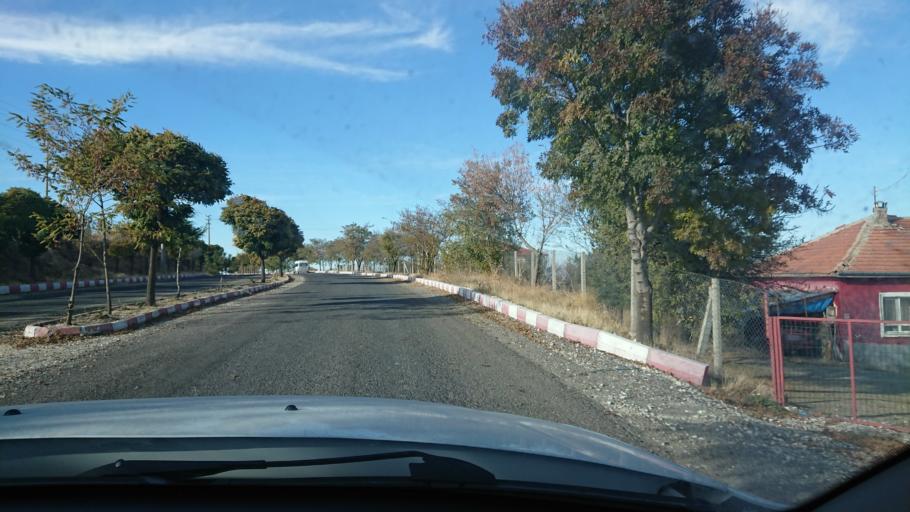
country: TR
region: Aksaray
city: Sariyahsi
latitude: 38.9653
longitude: 33.8749
